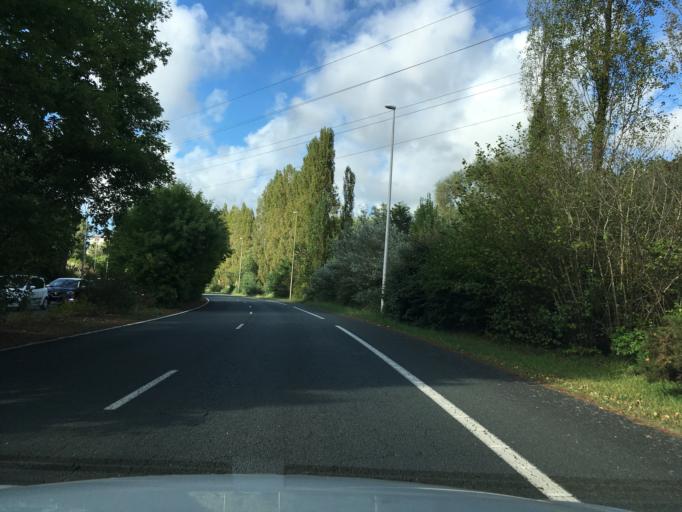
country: FR
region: Aquitaine
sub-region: Departement des Pyrenees-Atlantiques
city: Bayonne
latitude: 43.4728
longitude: -1.4899
